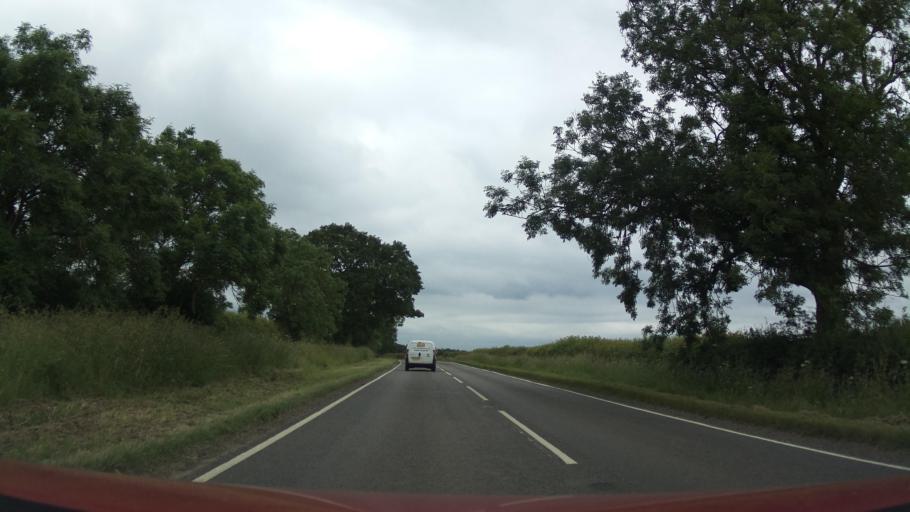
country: GB
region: England
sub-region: Leicestershire
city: Grimston
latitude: 52.7951
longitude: -1.0349
